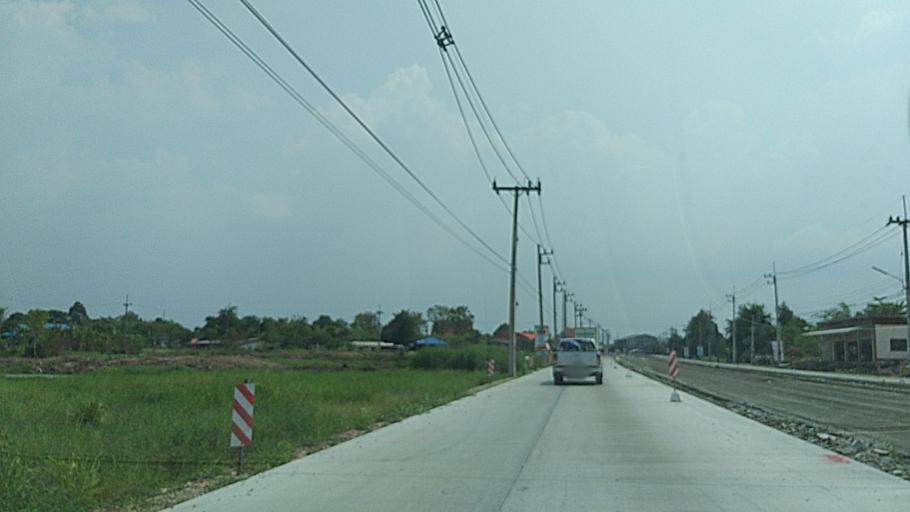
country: TH
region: Chon Buri
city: Phanat Nikhom
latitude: 13.4025
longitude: 101.1904
